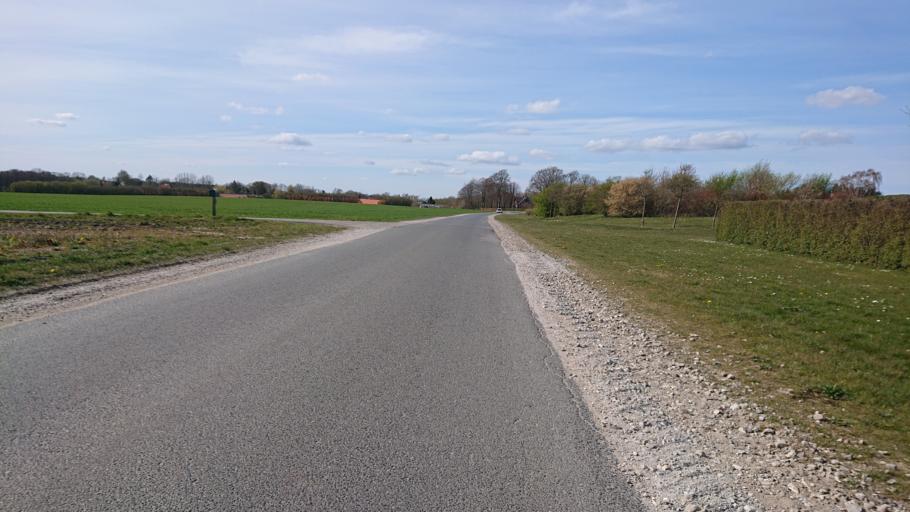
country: DK
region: South Denmark
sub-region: Nyborg Kommune
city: Nyborg
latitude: 55.3092
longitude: 10.7460
